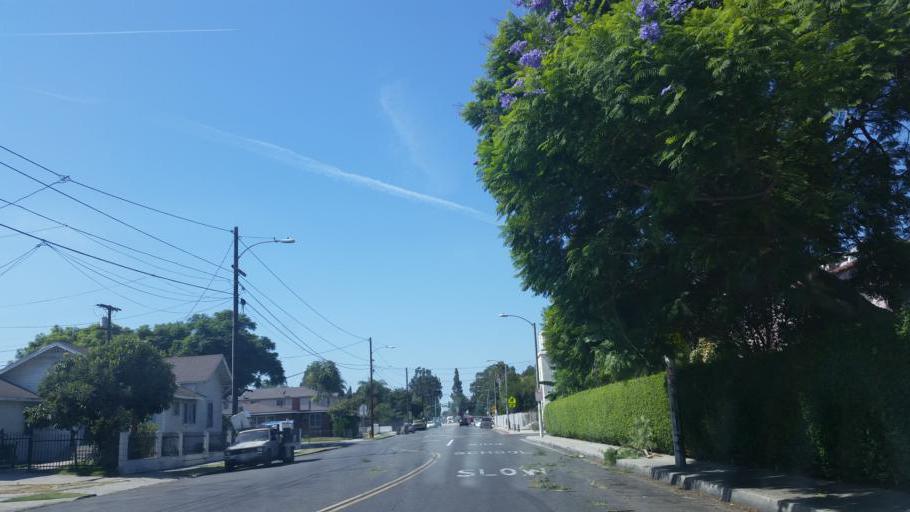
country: US
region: California
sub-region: Los Angeles County
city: Compton
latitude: 33.8924
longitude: -118.2210
